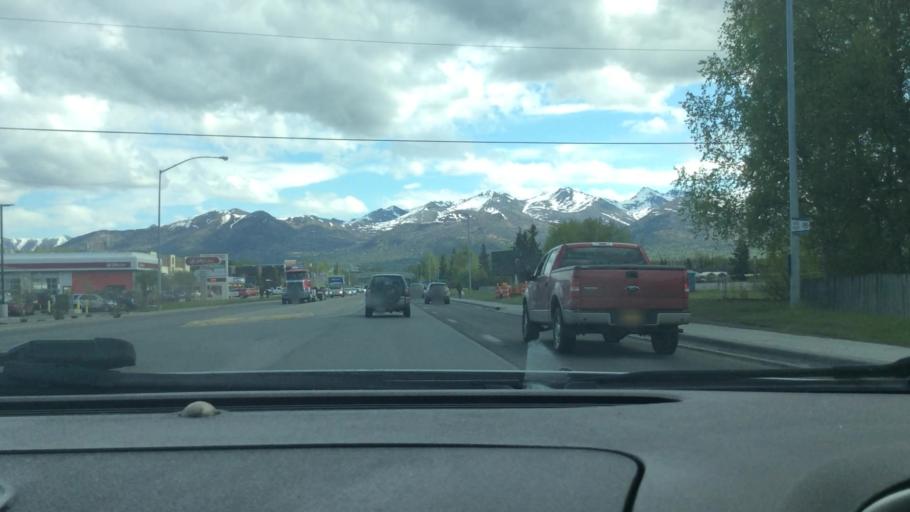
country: US
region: Alaska
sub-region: Anchorage Municipality
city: Anchorage
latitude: 61.1808
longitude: -149.8182
